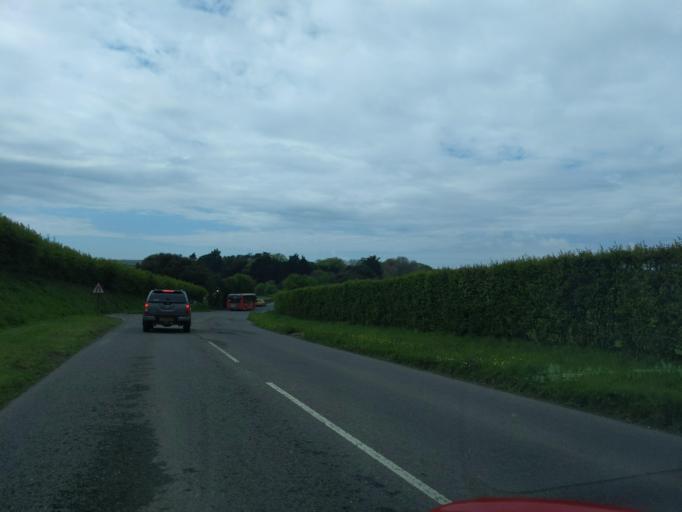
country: GB
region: England
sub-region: Cornwall
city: Wadebridge
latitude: 50.5329
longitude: -4.8395
